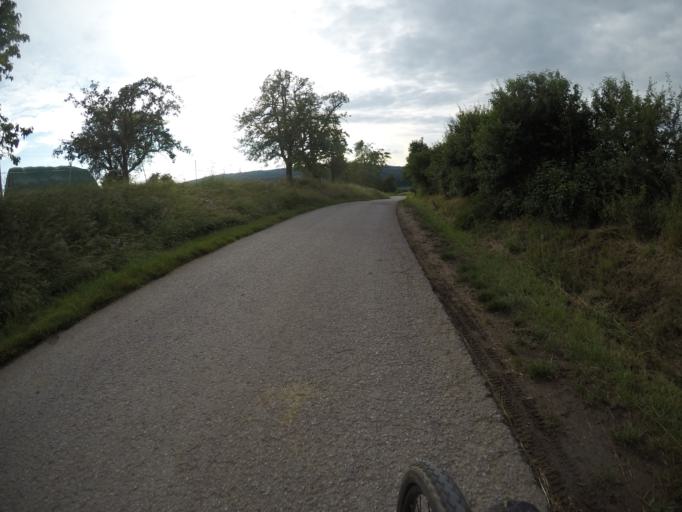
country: DE
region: Baden-Wuerttemberg
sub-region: Regierungsbezirk Stuttgart
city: Schlaitdorf
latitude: 48.6095
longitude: 9.2176
